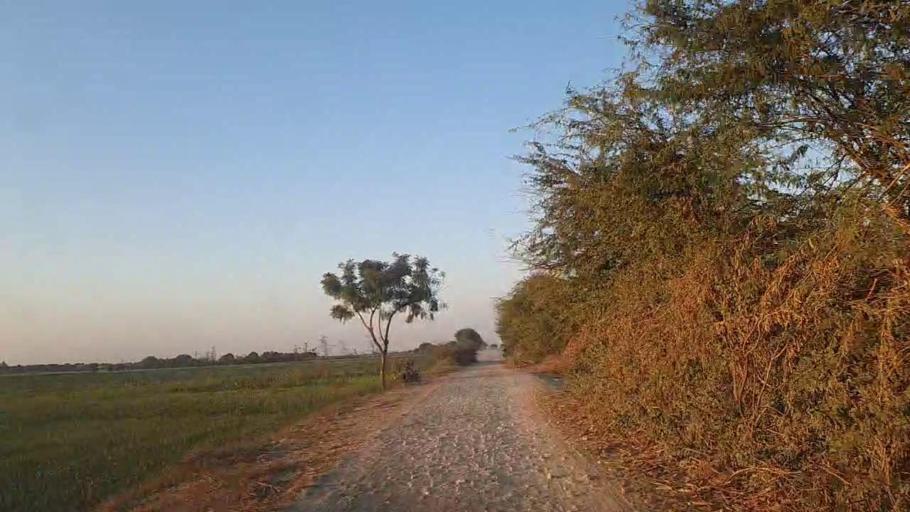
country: PK
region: Sindh
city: Naukot
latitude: 25.0527
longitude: 69.4070
